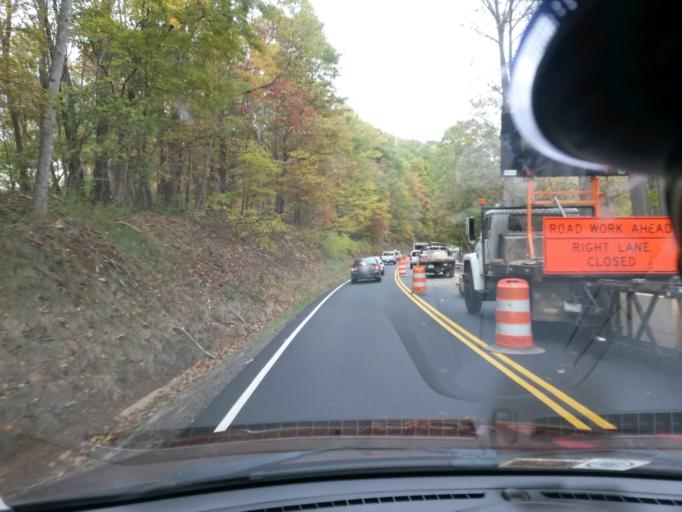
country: US
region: Virginia
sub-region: Roanoke County
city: Narrows
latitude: 37.1816
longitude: -79.8768
